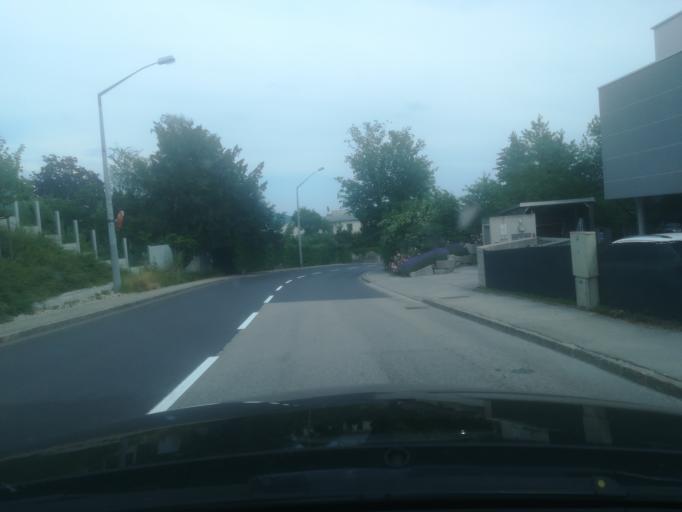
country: AT
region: Upper Austria
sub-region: Linz Stadt
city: Linz
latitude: 48.3129
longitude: 14.2608
